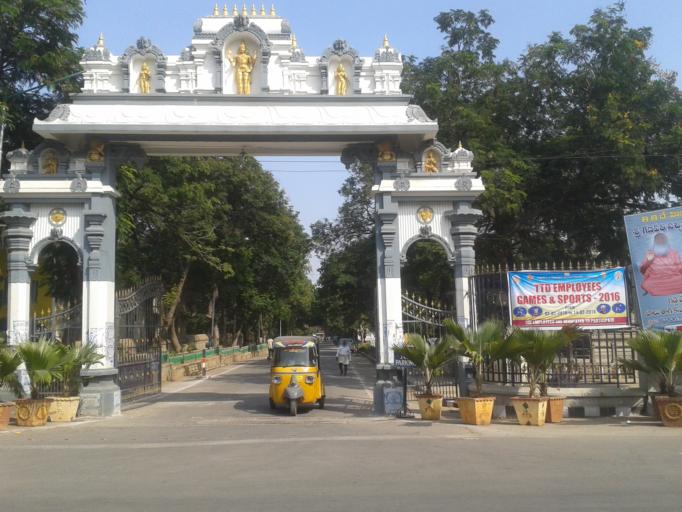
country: IN
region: Andhra Pradesh
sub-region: Chittoor
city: Tirupati
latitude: 13.6417
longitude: 79.4187
